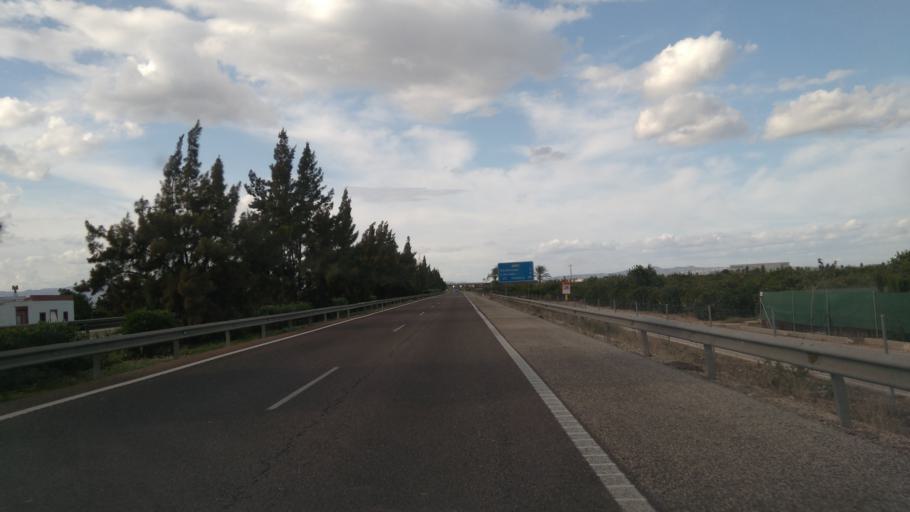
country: ES
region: Valencia
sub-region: Provincia de Valencia
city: Guadassuar
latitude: 39.1655
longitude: -0.4591
